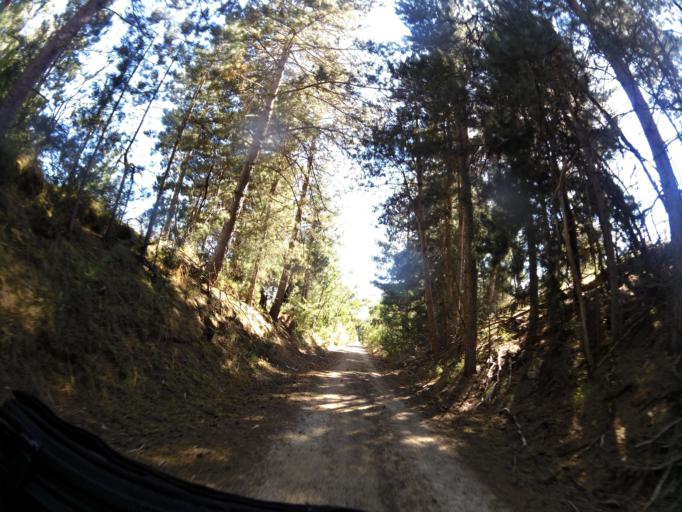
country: AU
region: Victoria
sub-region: Ballarat North
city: Delacombe
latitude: -37.6799
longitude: 143.4359
